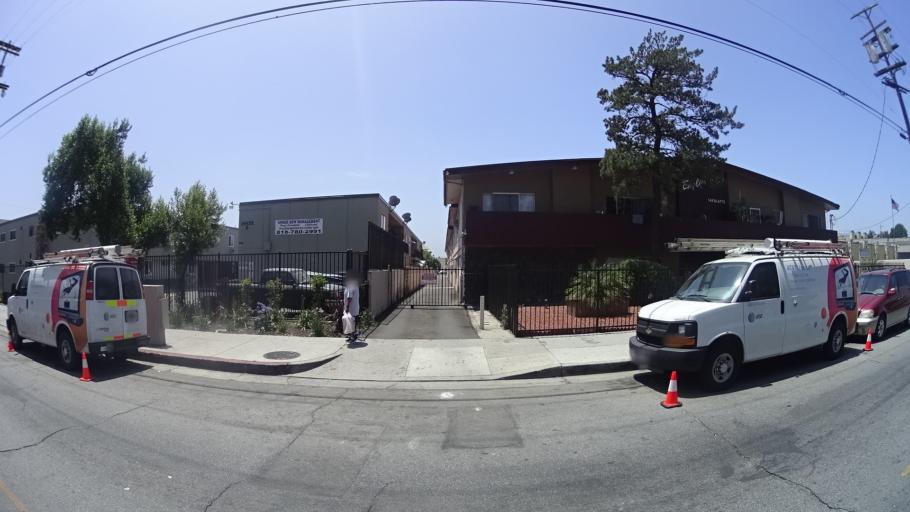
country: US
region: California
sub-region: Los Angeles County
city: Van Nuys
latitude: 34.2048
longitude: -118.4477
